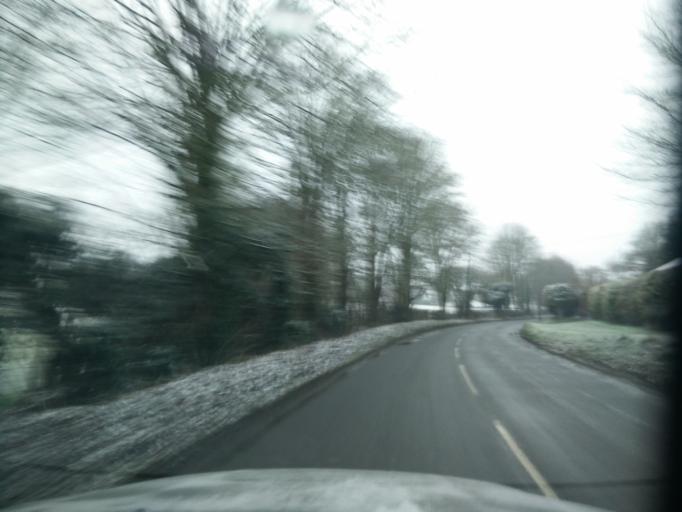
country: GB
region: England
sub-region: Buckinghamshire
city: Princes Risborough
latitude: 51.7357
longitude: -0.8091
